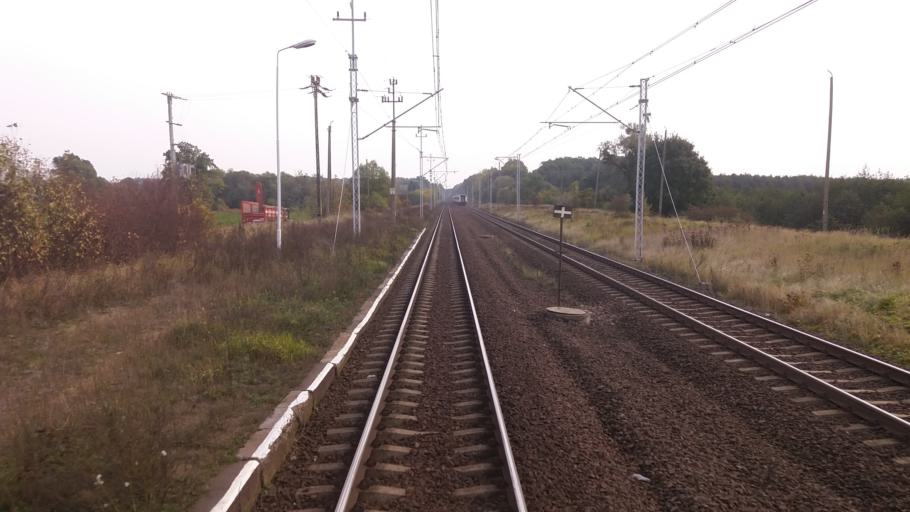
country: PL
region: West Pomeranian Voivodeship
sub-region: Powiat stargardzki
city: Dolice
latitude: 53.1664
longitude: 15.3058
